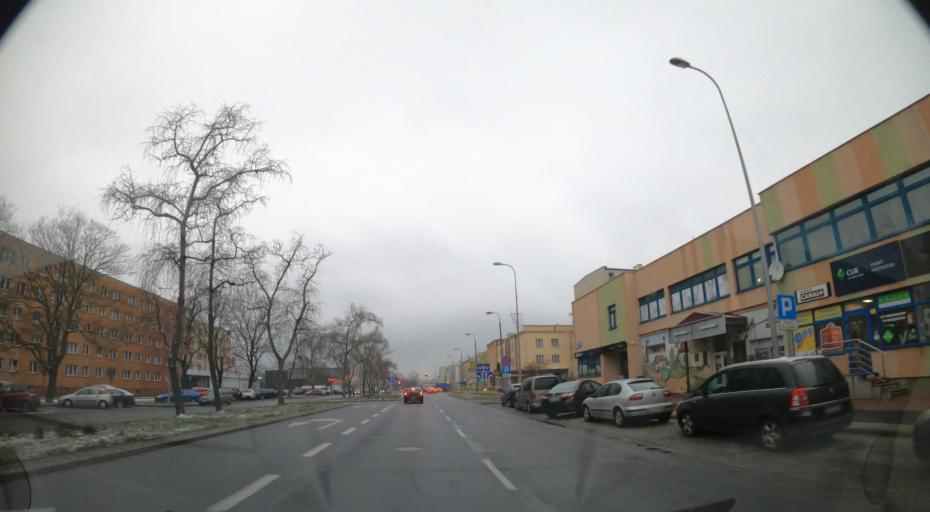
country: PL
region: Masovian Voivodeship
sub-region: Plock
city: Plock
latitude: 52.5488
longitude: 19.6965
